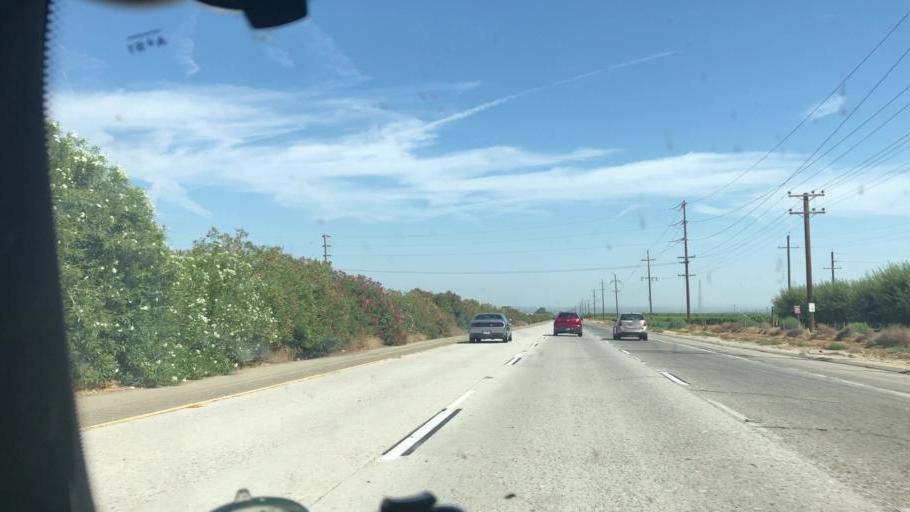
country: US
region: California
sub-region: Kern County
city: Frazier Park
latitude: 35.0256
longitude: -118.9576
